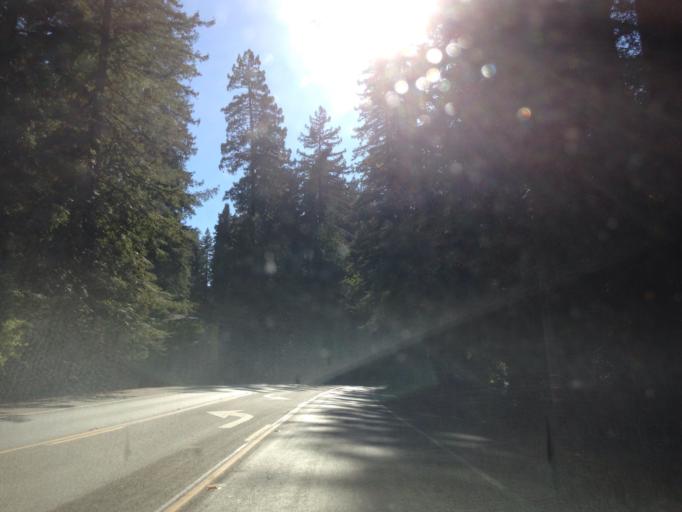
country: US
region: California
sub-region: Sonoma County
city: Guerneville
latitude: 38.4951
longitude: -123.0091
